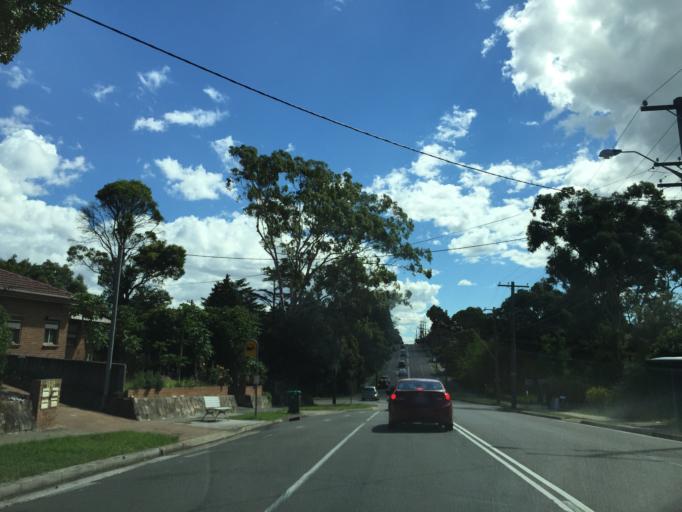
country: AU
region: New South Wales
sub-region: Ryde
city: Marsfield
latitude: -33.7810
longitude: 151.1009
